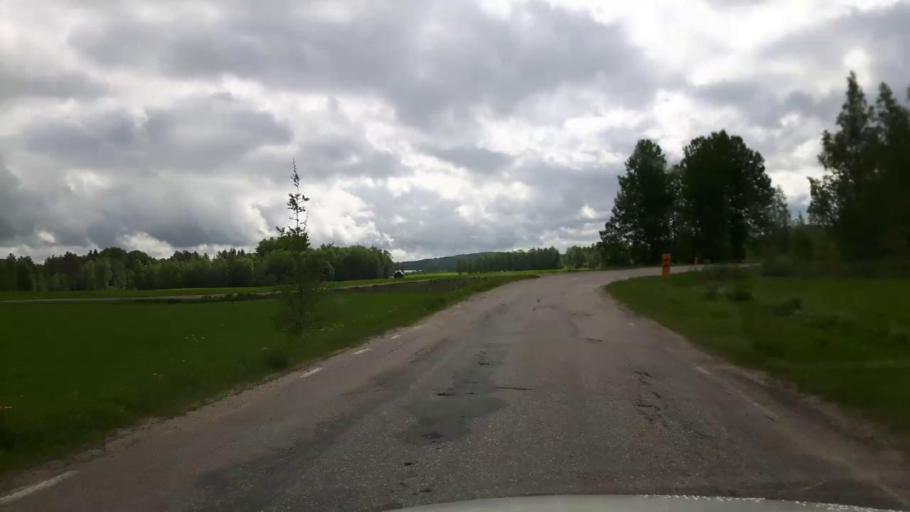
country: SE
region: Gaevleborg
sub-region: Ovanakers Kommun
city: Edsbyn
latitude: 61.3527
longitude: 15.9170
